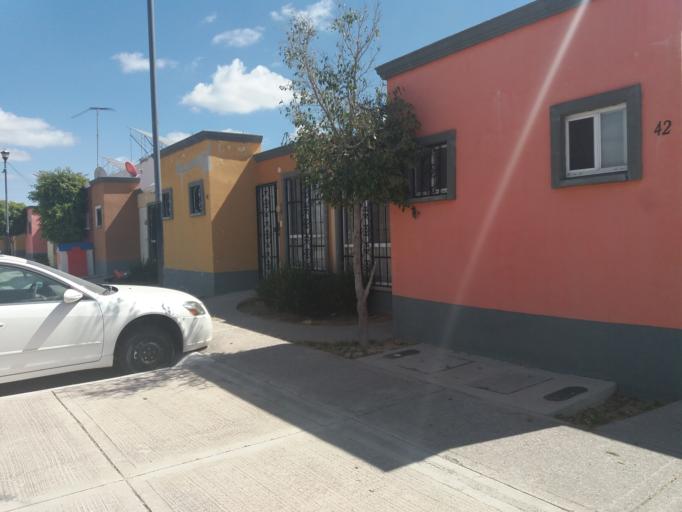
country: MX
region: Aguascalientes
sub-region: Aguascalientes
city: San Sebastian [Fraccionamiento]
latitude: 21.7941
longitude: -102.2754
